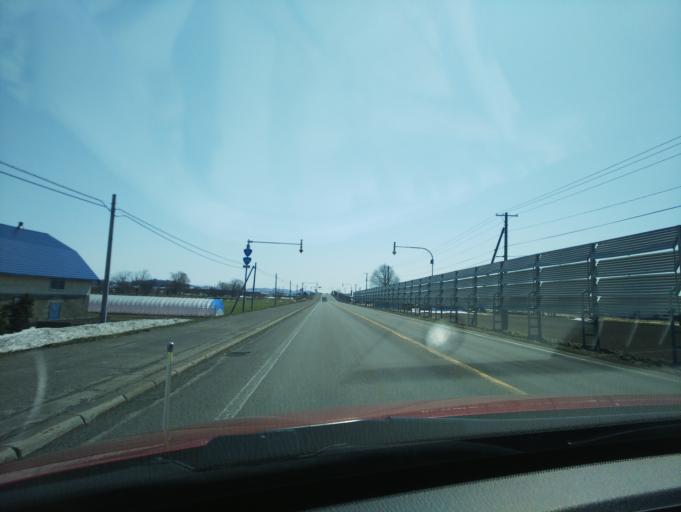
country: JP
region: Hokkaido
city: Nayoro
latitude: 44.1999
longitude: 142.3949
